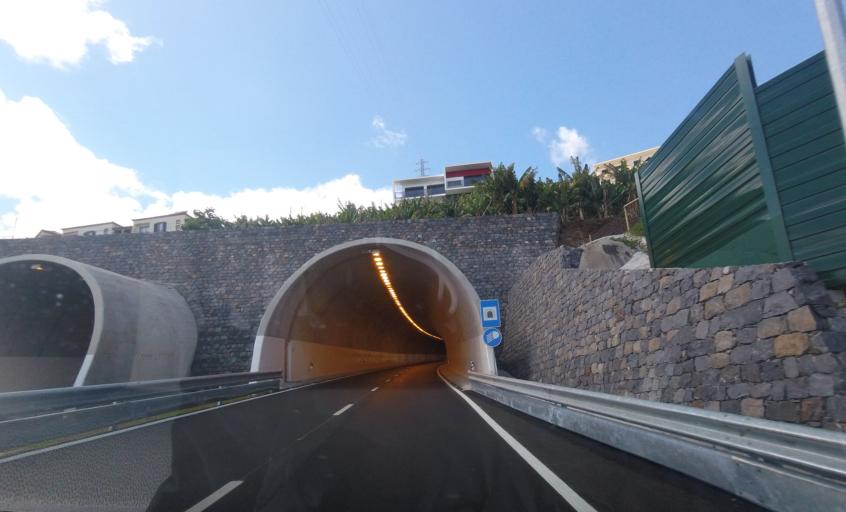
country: PT
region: Madeira
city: Camara de Lobos
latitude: 32.6636
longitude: -16.9689
